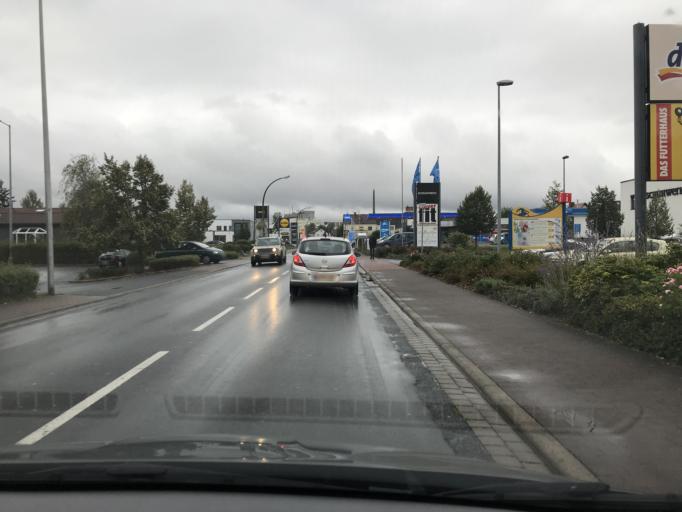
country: DE
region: Bavaria
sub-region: Regierungsbezirk Unterfranken
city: Grossostheim
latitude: 49.9272
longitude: 9.0808
